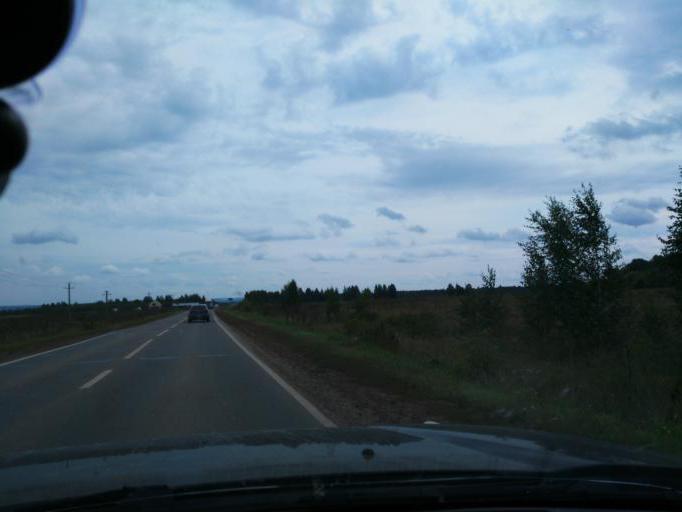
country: RU
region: Perm
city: Chernushka
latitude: 56.5089
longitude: 55.9732
